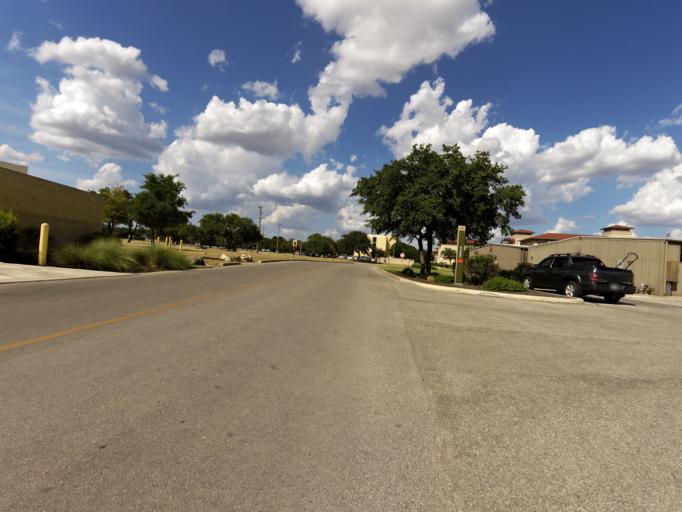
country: US
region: Texas
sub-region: Bexar County
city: Helotes
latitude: 29.5835
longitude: -98.6286
